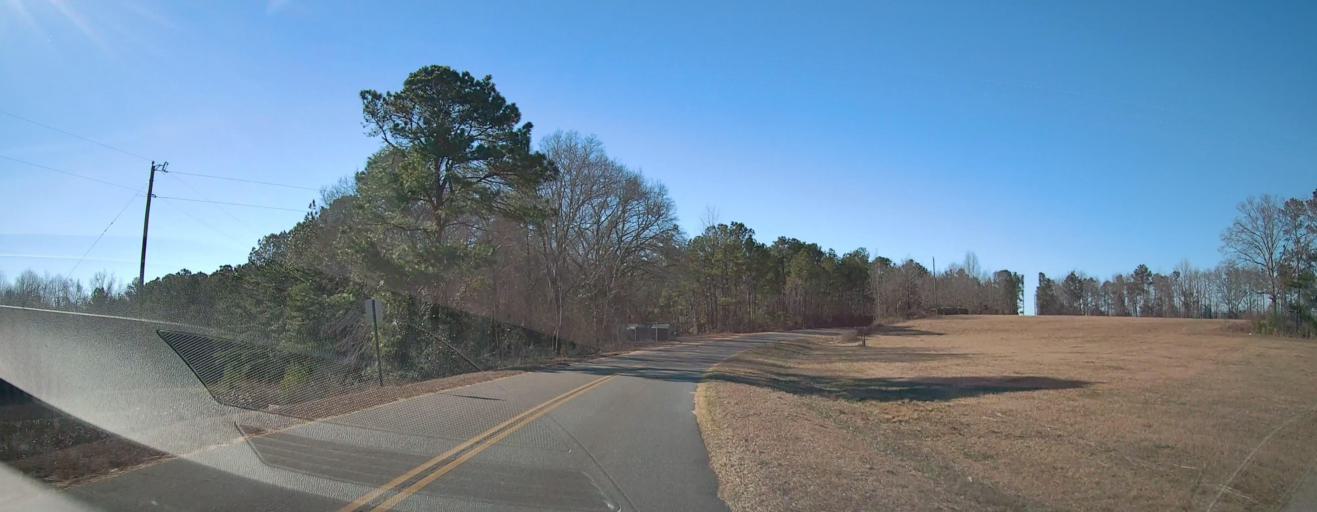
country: US
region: Georgia
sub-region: Taylor County
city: Butler
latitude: 32.6443
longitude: -84.3138
